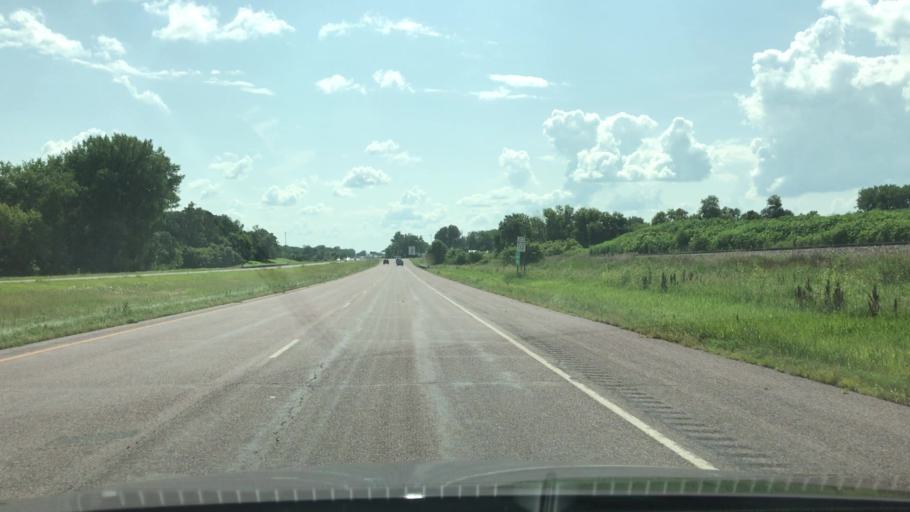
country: US
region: Minnesota
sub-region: Blue Earth County
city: Lake Crystal
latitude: 44.1194
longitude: -94.2030
